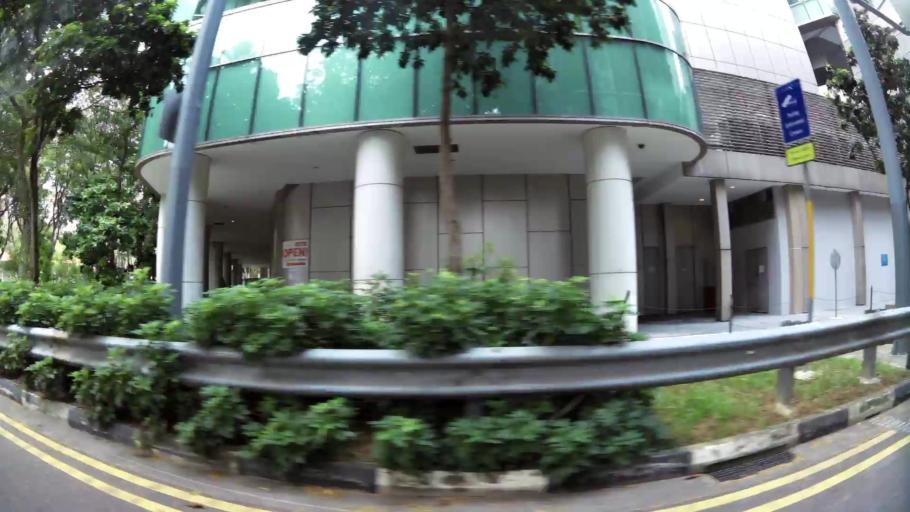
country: SG
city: Singapore
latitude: 1.2735
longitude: 103.8420
